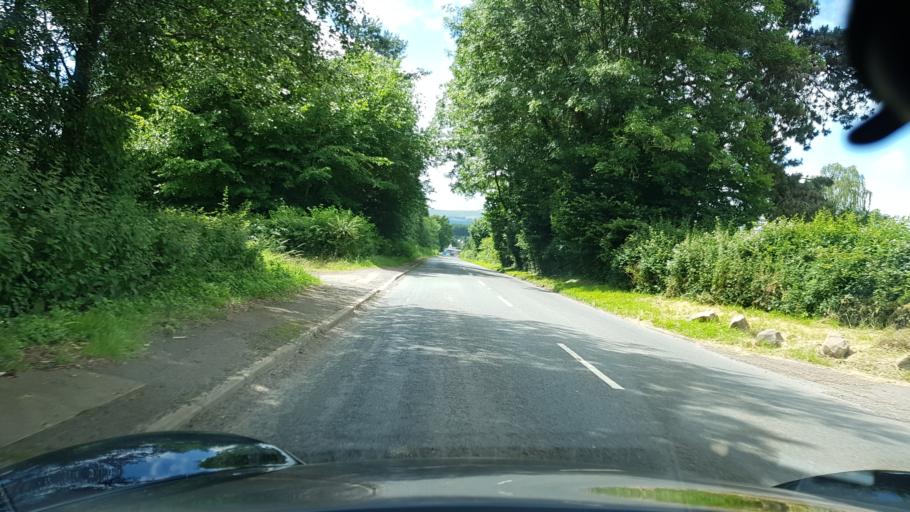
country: GB
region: Wales
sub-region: Monmouthshire
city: Llanarth
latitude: 51.7851
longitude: -2.9591
